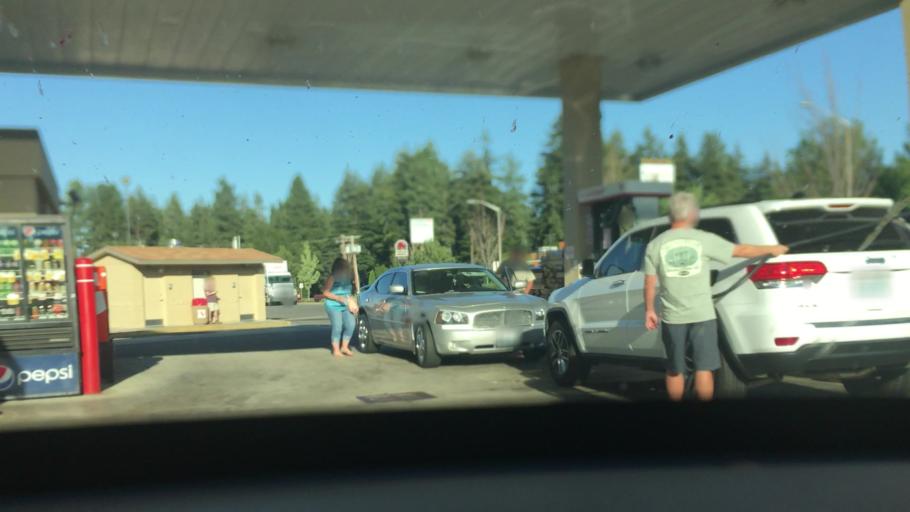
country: US
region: Washington
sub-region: Kittitas County
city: Cle Elum
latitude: 47.1951
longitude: -120.9550
